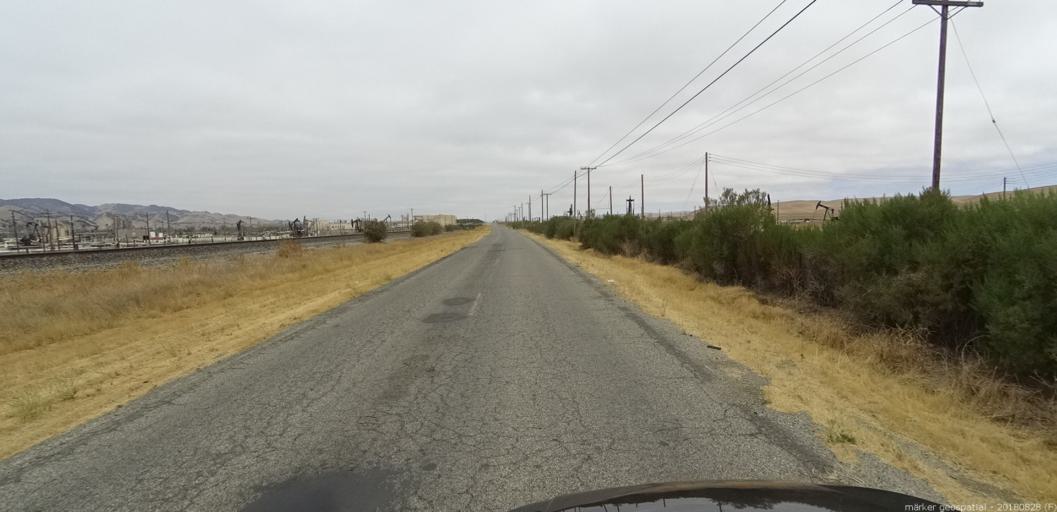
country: US
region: California
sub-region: San Luis Obispo County
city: Lake Nacimiento
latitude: 35.9604
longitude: -120.8669
